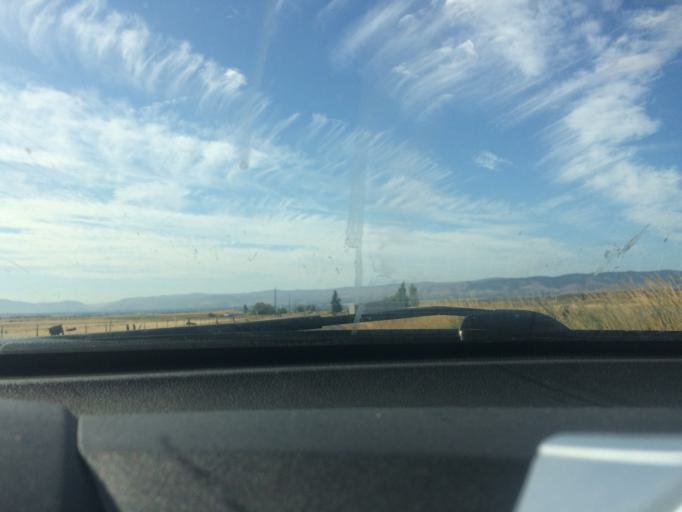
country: US
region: Washington
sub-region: Kittitas County
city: Ellensburg
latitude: 47.0903
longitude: -120.6034
